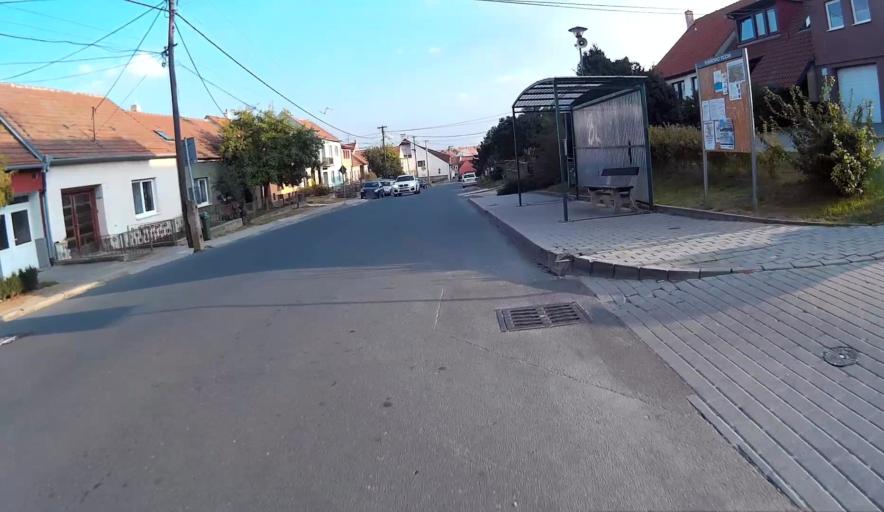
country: CZ
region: South Moravian
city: Podoli
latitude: 49.1919
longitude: 16.7198
